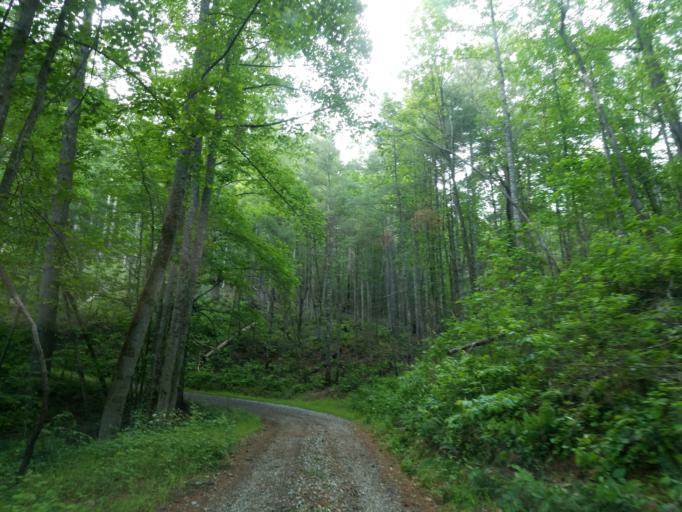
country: US
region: Georgia
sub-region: Union County
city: Blairsville
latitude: 34.7579
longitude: -84.0348
